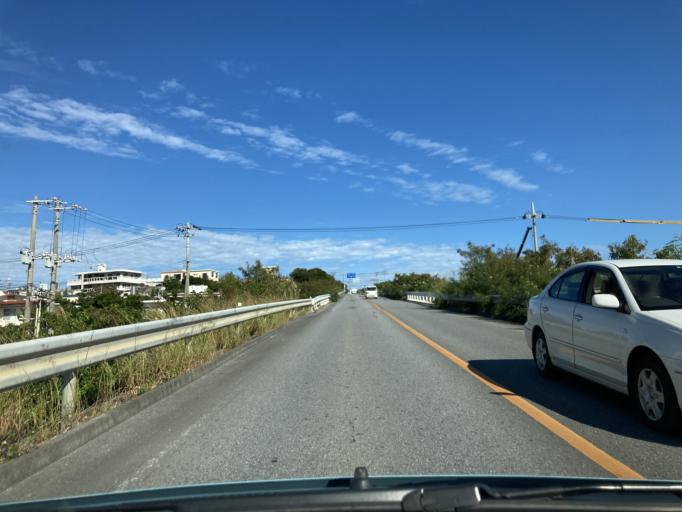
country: JP
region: Okinawa
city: Okinawa
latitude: 26.3801
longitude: 127.7455
